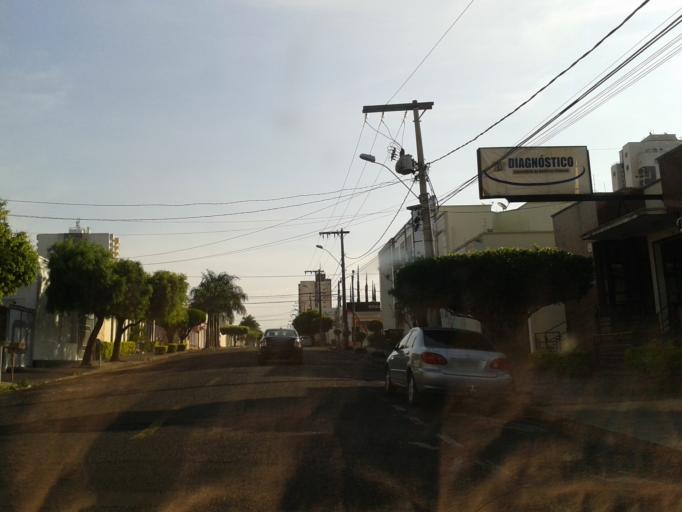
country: BR
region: Minas Gerais
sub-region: Araguari
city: Araguari
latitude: -18.6492
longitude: -48.1872
